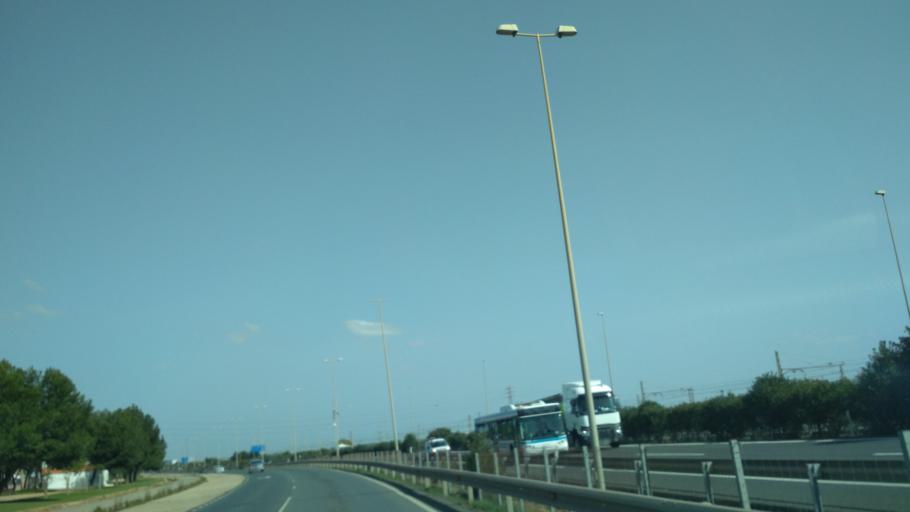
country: ES
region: Andalusia
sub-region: Provincia de Huelva
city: Huelva
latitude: 37.2534
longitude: -6.9297
